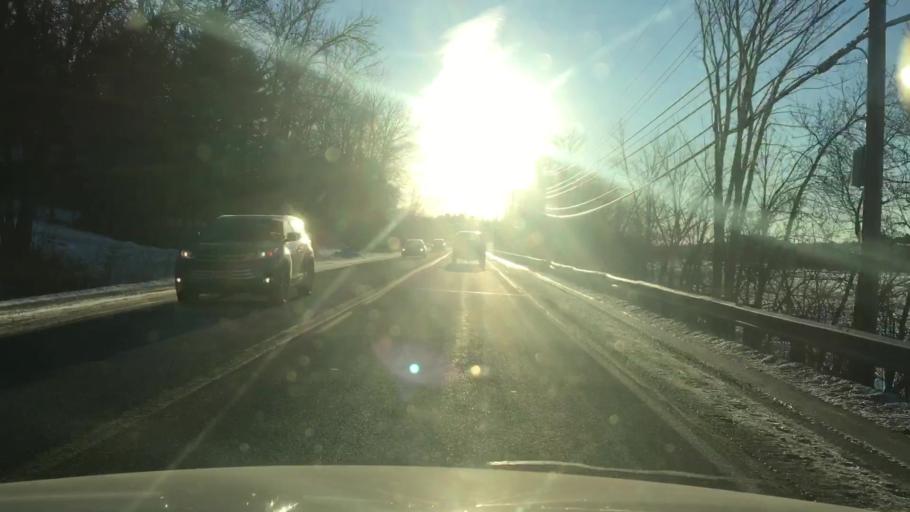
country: US
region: Maine
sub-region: Penobscot County
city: Veazie
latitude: 44.8146
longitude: -68.7302
